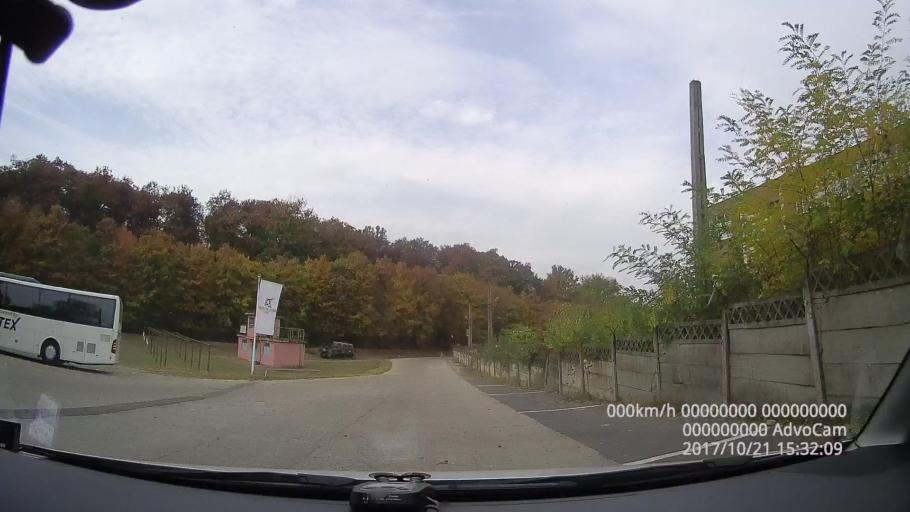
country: RO
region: Hunedoara
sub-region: Comuna Soimus
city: Soimus
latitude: 45.9000
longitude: 22.8893
